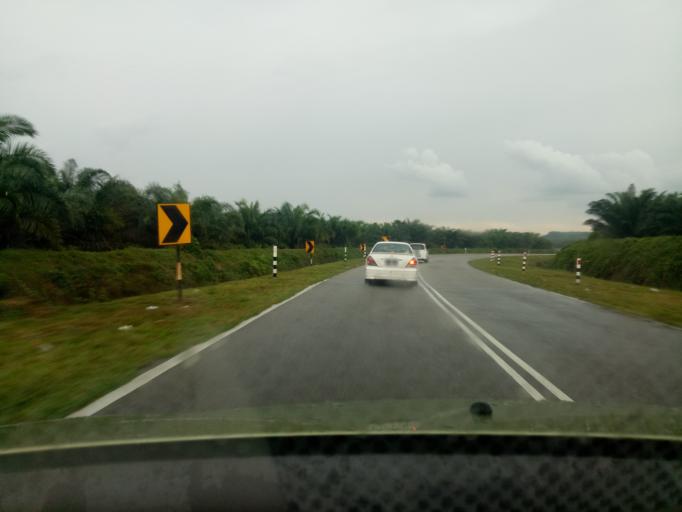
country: MY
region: Penang
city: Tasek Glugor
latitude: 5.5097
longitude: 100.5706
